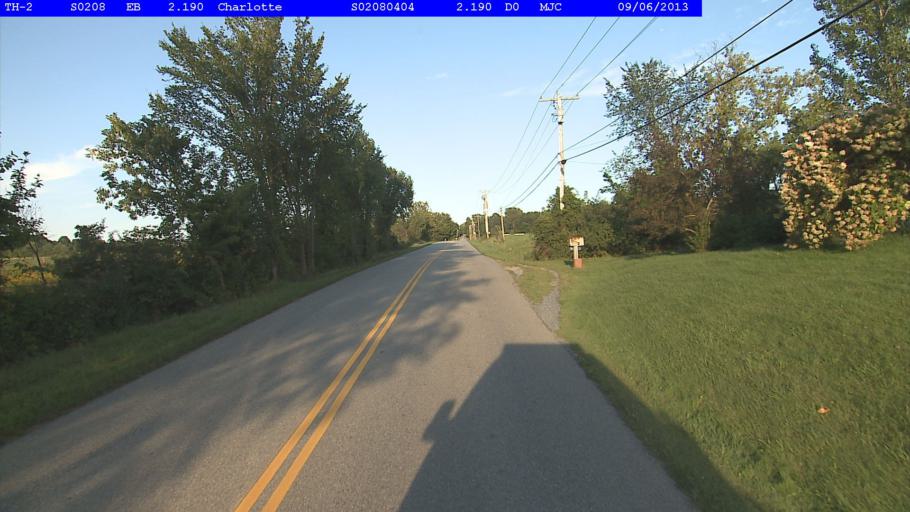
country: US
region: Vermont
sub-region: Chittenden County
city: Hinesburg
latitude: 44.3181
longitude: -73.2047
